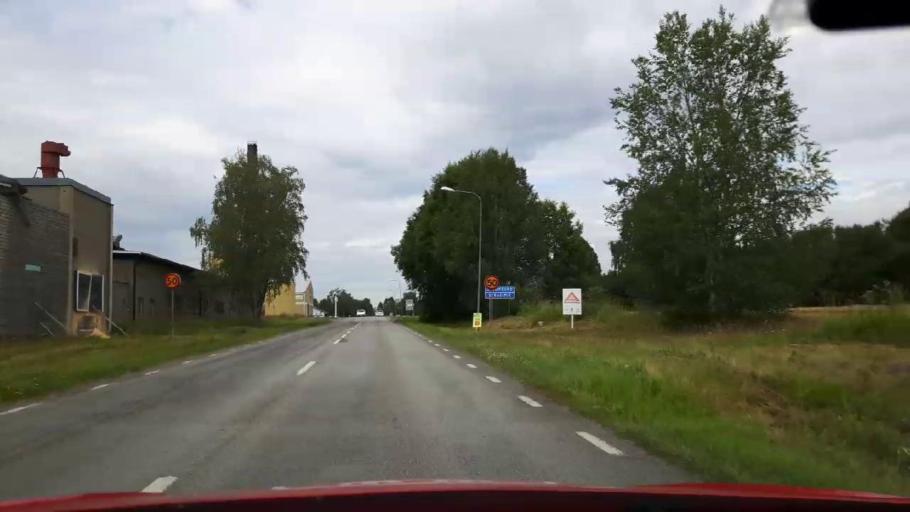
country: SE
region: Jaemtland
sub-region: Stroemsunds Kommun
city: Stroemsund
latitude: 63.8465
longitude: 15.5730
